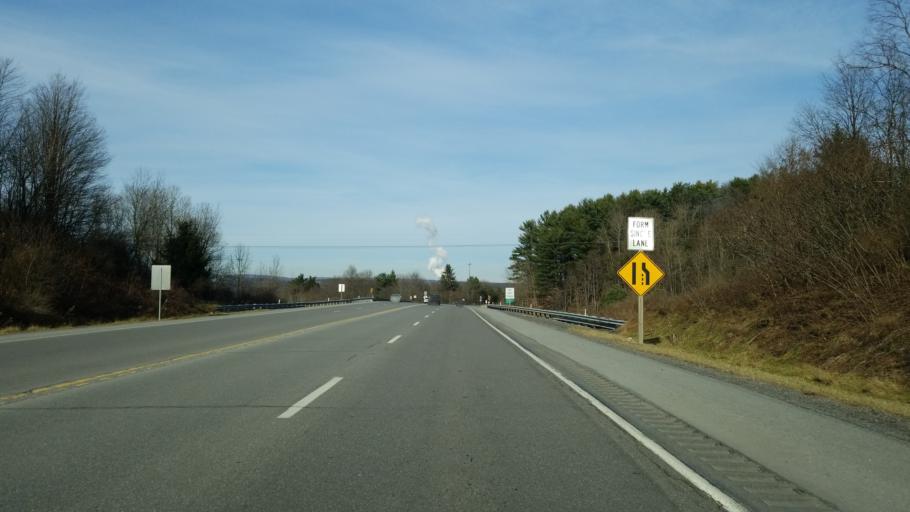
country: US
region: Pennsylvania
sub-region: Clearfield County
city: Clearfield
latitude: 41.0158
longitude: -78.4280
